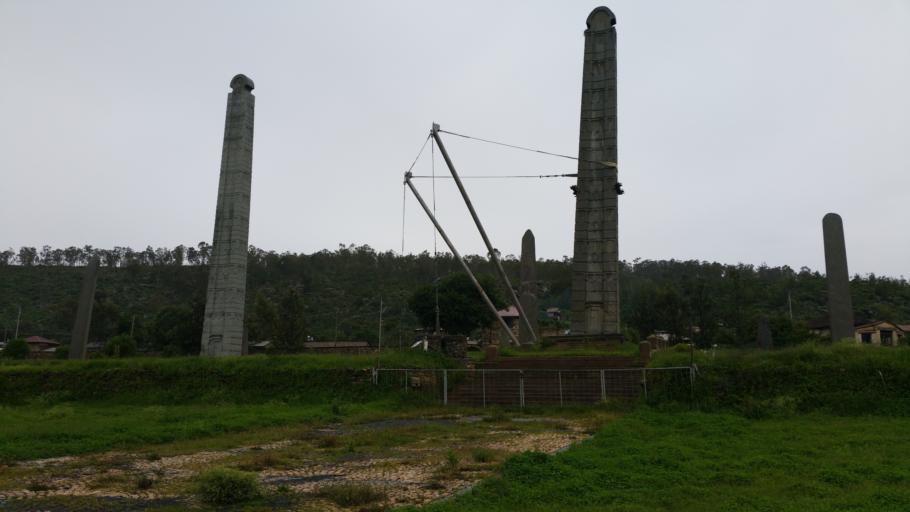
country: ET
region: Tigray
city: Aksum
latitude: 14.1317
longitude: 38.7196
